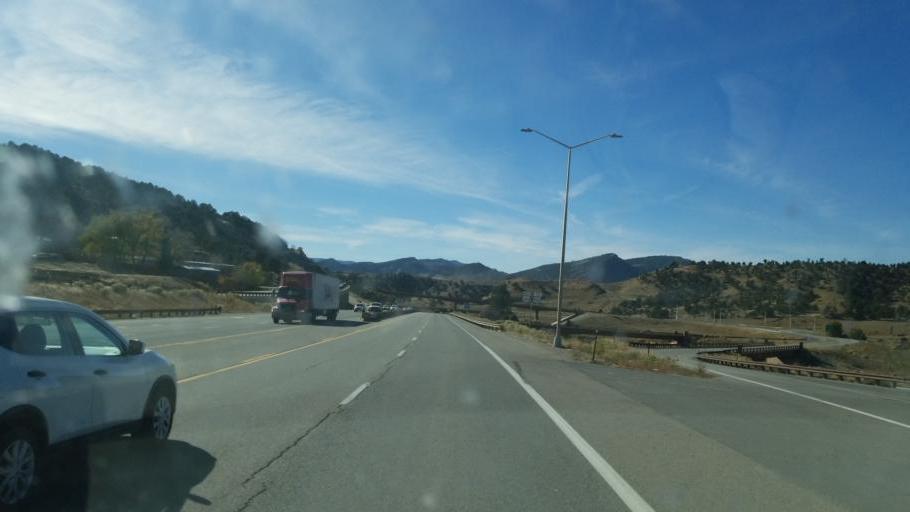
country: US
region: Colorado
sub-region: La Plata County
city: Durango
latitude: 37.2290
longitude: -107.8331
